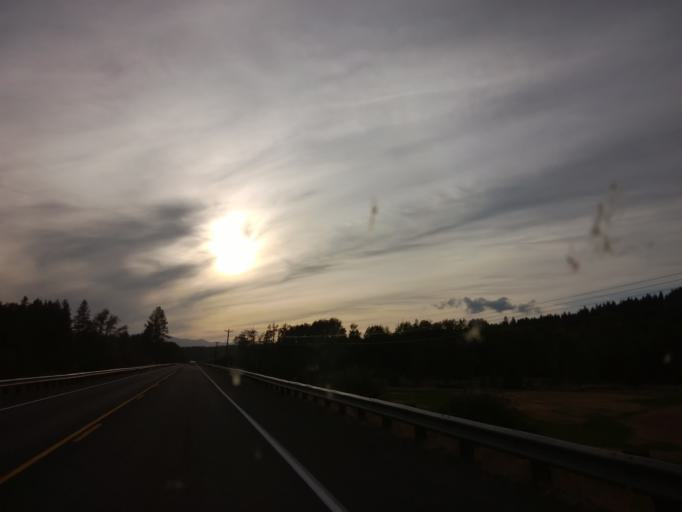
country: US
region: Washington
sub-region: Kittitas County
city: Cle Elum
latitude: 47.1961
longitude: -120.7813
